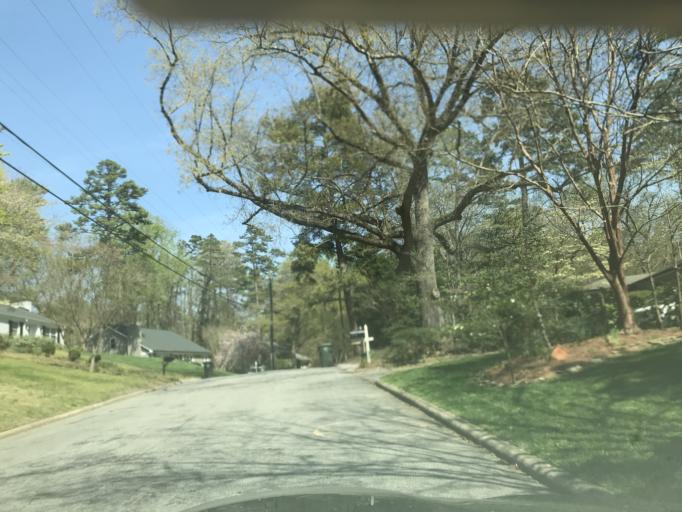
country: US
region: North Carolina
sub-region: Wake County
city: West Raleigh
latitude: 35.8250
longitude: -78.6372
